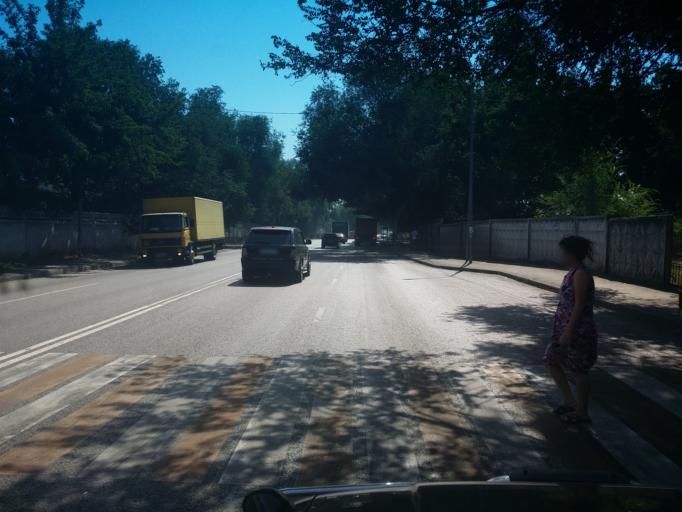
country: KZ
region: Almaty Oblysy
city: Pervomayskiy
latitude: 43.3483
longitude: 76.9654
